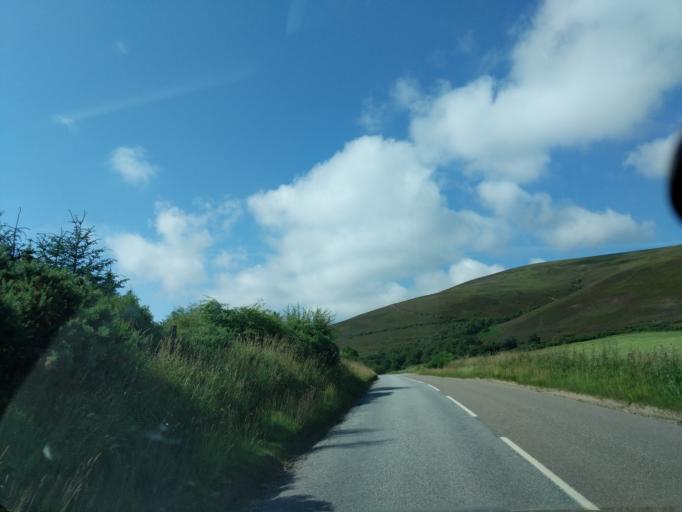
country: GB
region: Scotland
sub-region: Moray
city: Dufftown
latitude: 57.4244
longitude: -3.1581
